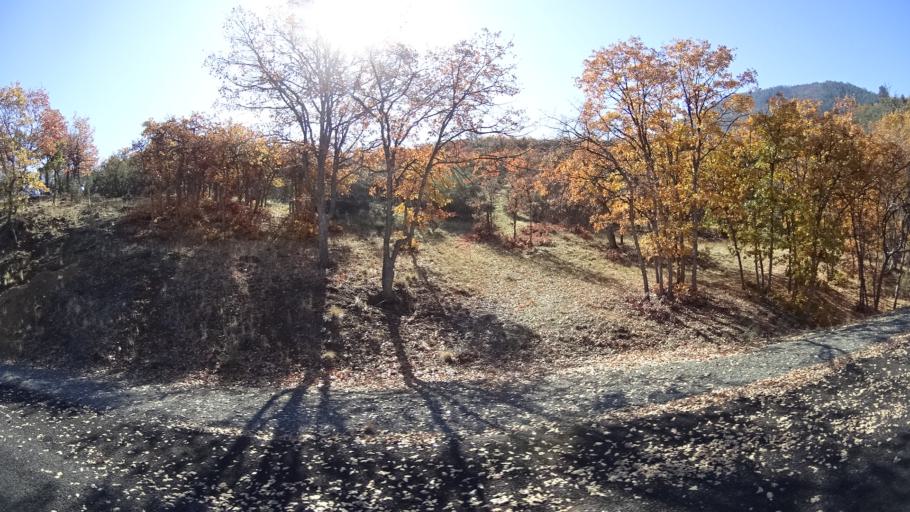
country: US
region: California
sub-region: Siskiyou County
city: Montague
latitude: 41.8773
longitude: -122.4915
